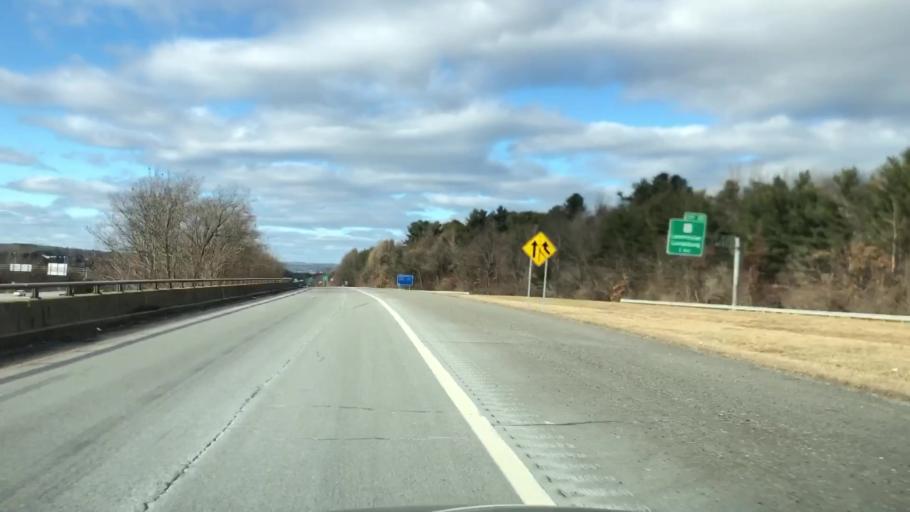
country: US
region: Massachusetts
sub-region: Worcester County
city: Leominster
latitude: 42.5248
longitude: -71.7283
